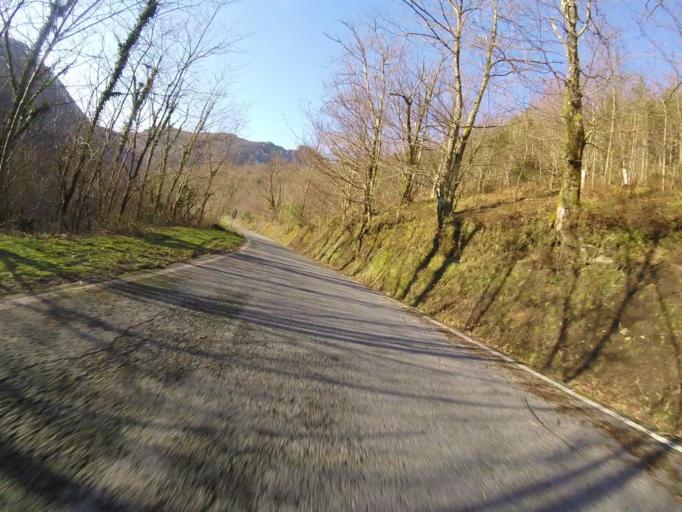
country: ES
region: Navarre
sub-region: Provincia de Navarra
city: Lesaka
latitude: 43.2684
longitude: -1.7686
